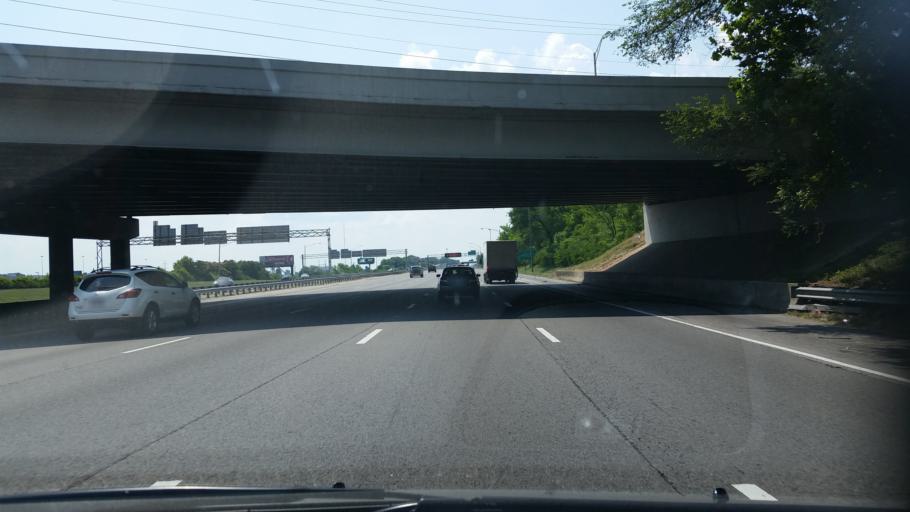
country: US
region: Tennessee
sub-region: Davidson County
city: Oak Hill
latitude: 36.1113
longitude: -86.7717
